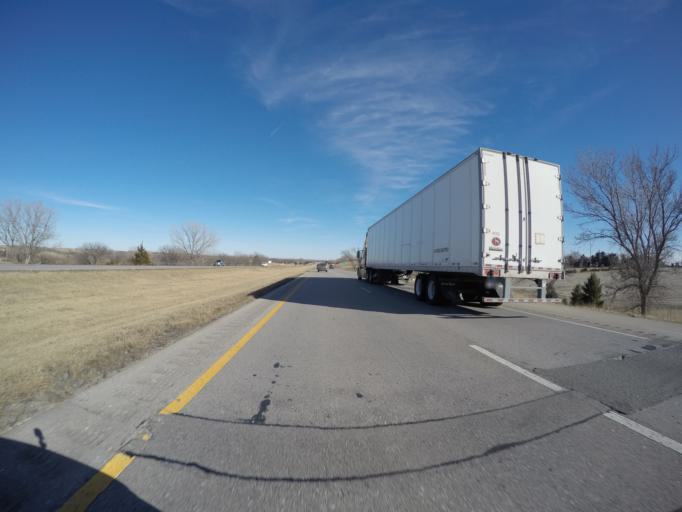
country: US
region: Nebraska
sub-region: Seward County
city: Milford
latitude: 40.8204
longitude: -96.9125
